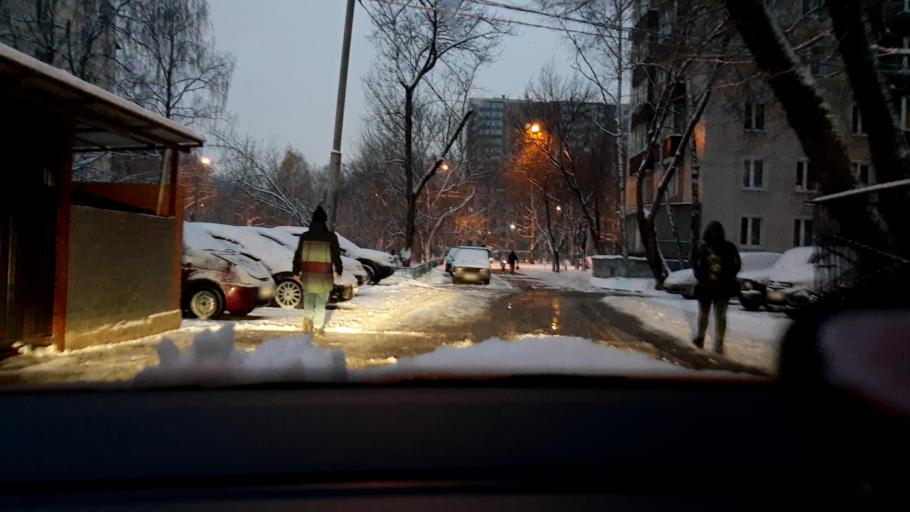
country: RU
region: Moscow
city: Novokuz'minki
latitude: 55.7056
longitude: 37.7816
